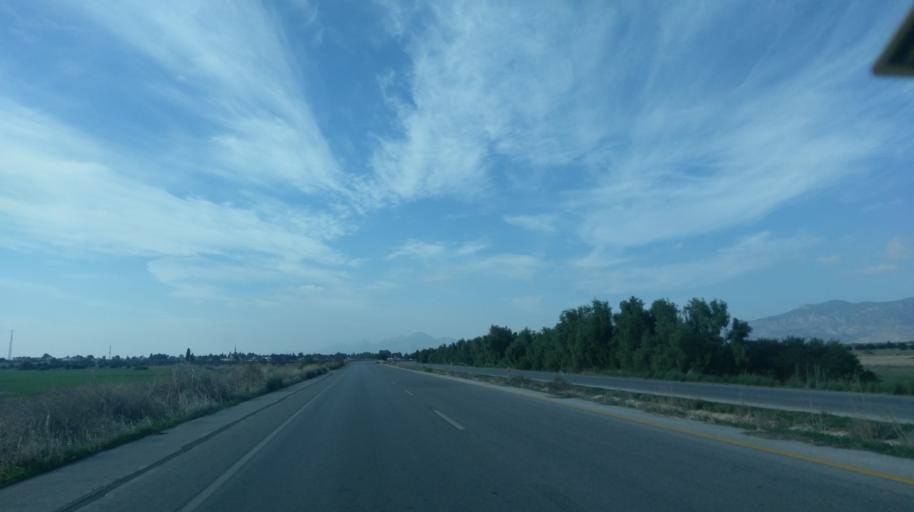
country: CY
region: Ammochostos
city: Lefkonoiko
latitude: 35.2016
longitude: 33.6034
